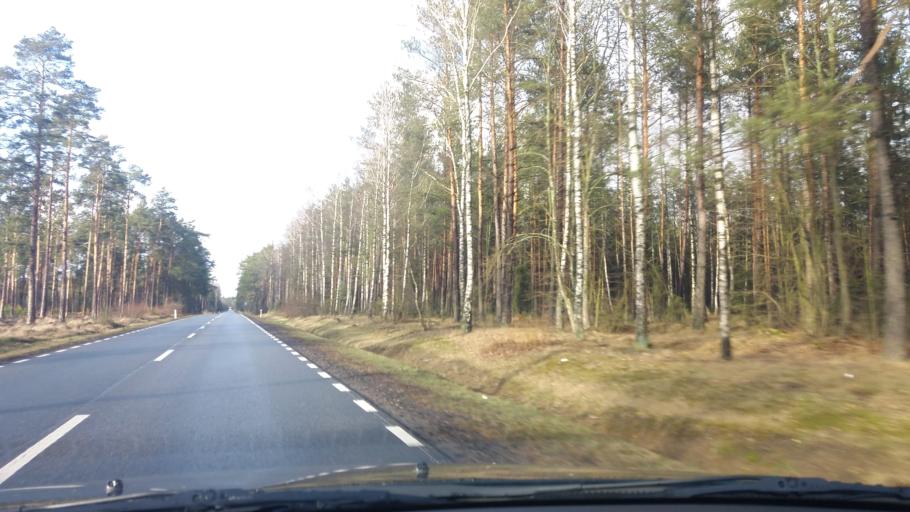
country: PL
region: Masovian Voivodeship
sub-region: Powiat przasnyski
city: Chorzele
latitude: 53.3046
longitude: 20.9125
